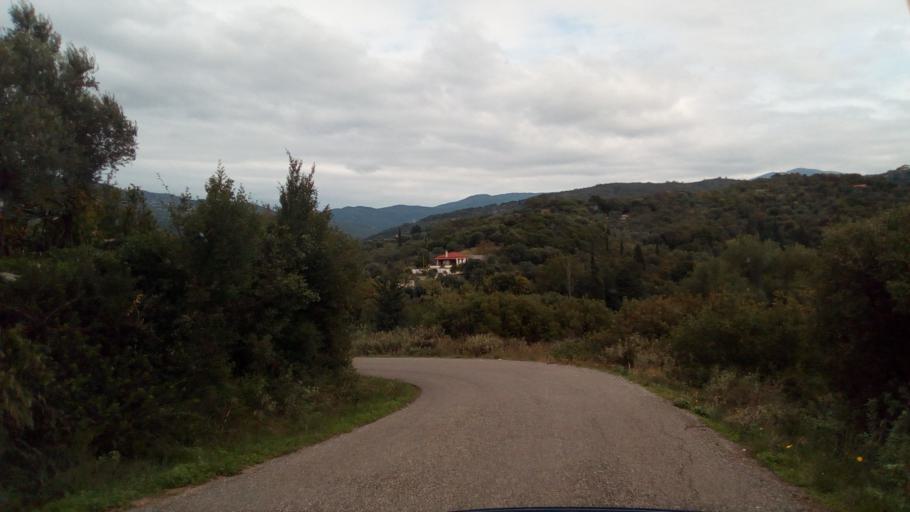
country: GR
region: West Greece
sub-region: Nomos Achaias
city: Kamarai
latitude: 38.4111
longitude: 21.9540
